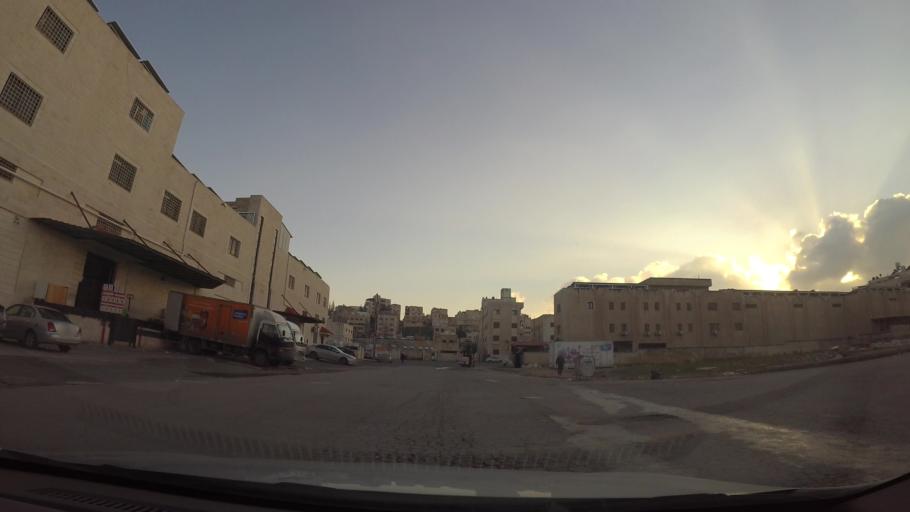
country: JO
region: Amman
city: Al Bunayyat ash Shamaliyah
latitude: 31.9090
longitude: 35.9185
